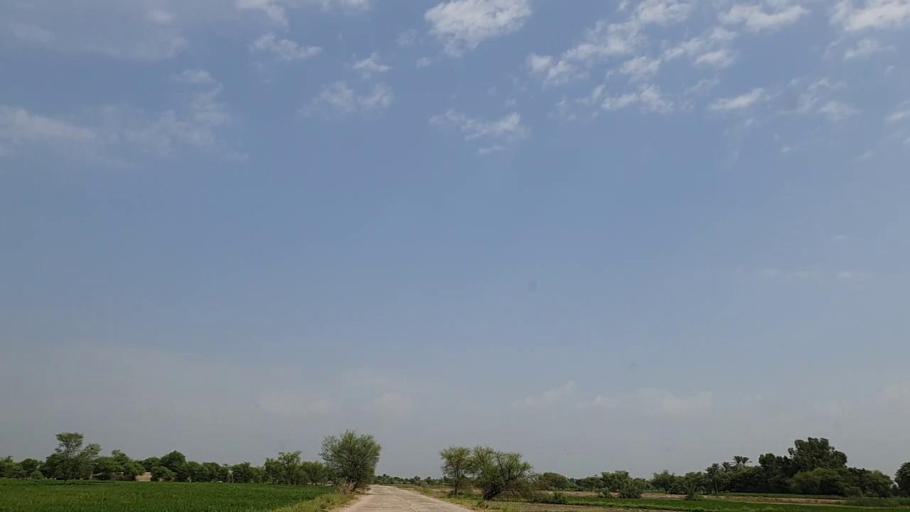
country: PK
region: Sindh
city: Khanpur
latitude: 27.8395
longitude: 69.4681
